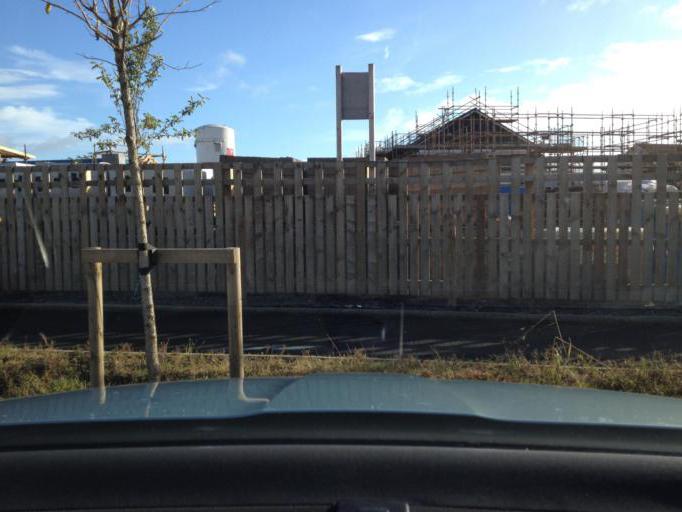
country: GB
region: Scotland
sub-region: West Lothian
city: East Calder
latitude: 55.9015
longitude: -3.4568
